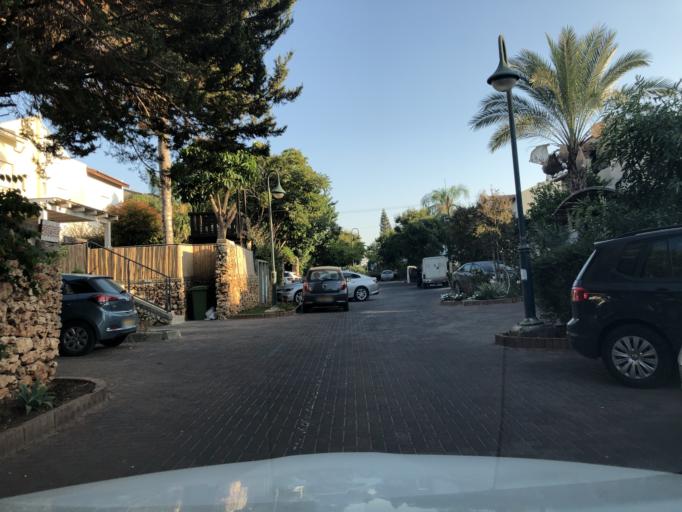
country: PS
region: West Bank
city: Hablah
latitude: 32.1611
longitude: 34.9717
